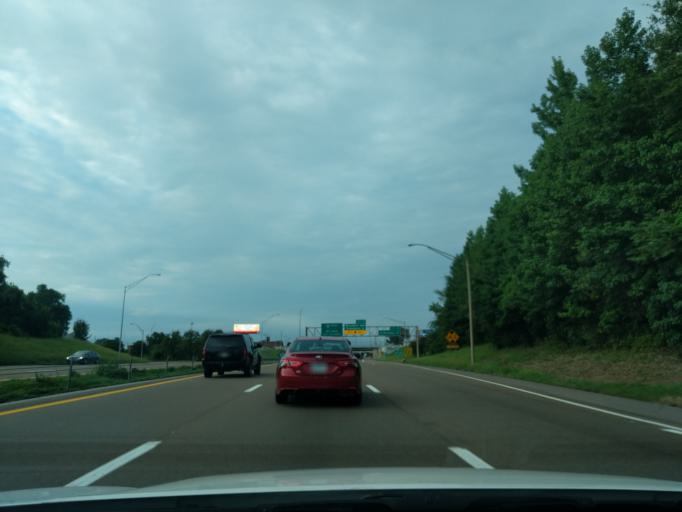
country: US
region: Tennessee
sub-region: Shelby County
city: New South Memphis
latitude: 35.1052
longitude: -90.0759
